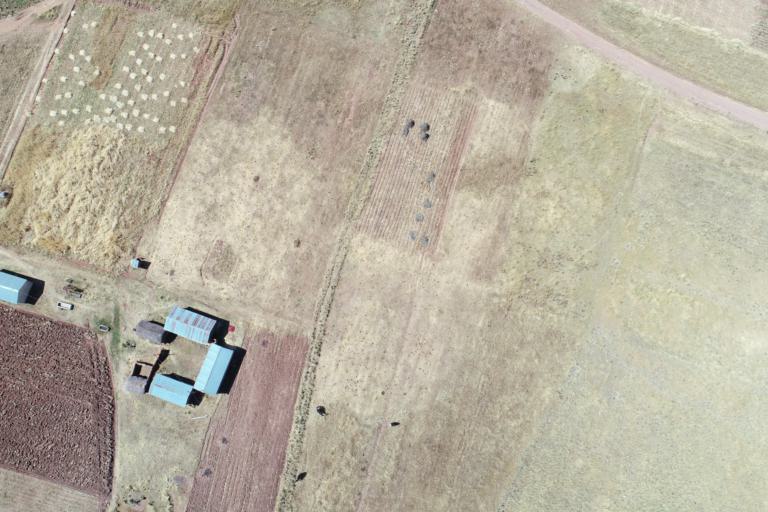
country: BO
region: La Paz
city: Tiahuanaco
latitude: -16.5931
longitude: -68.7727
